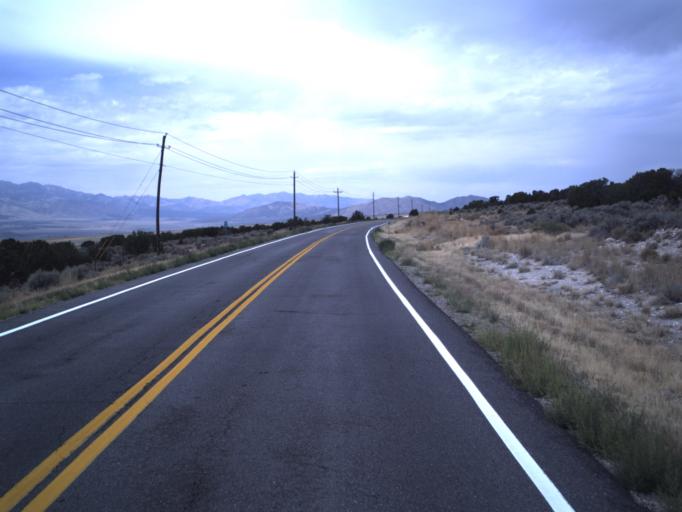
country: US
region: Utah
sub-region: Tooele County
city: Tooele
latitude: 40.3327
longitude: -112.2966
